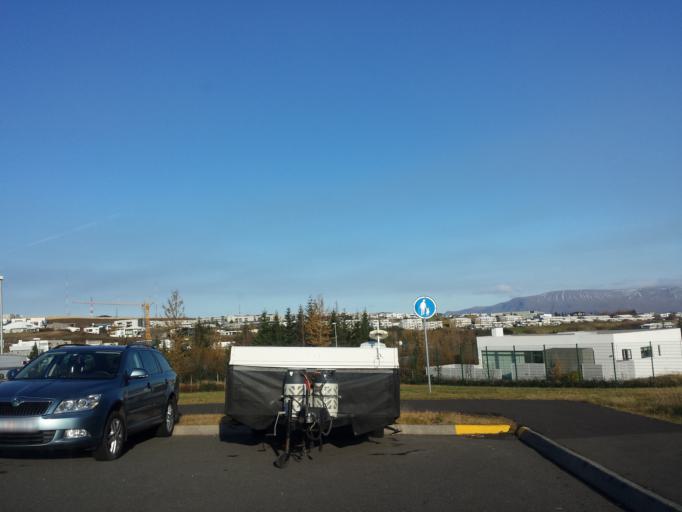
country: IS
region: Capital Region
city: Reykjavik
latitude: 64.0808
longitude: -21.8074
